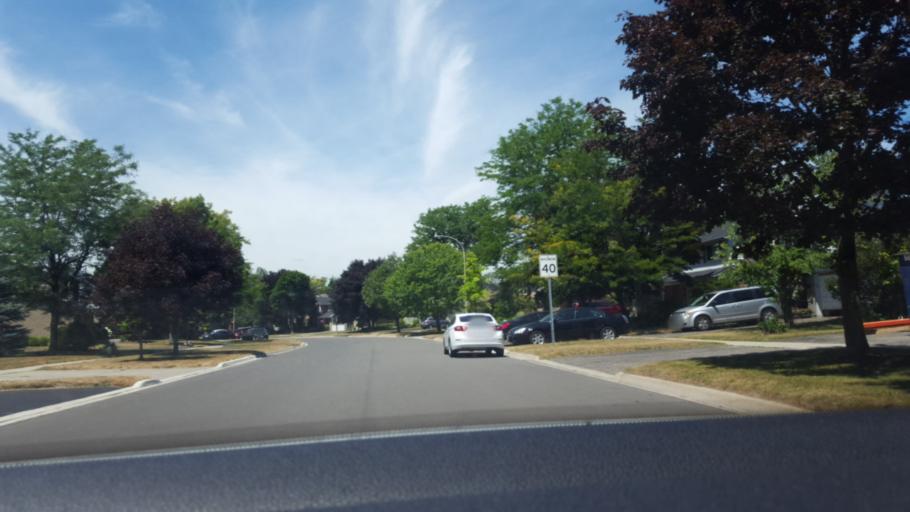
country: CA
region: Ontario
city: Ancaster
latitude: 43.2068
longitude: -79.9912
